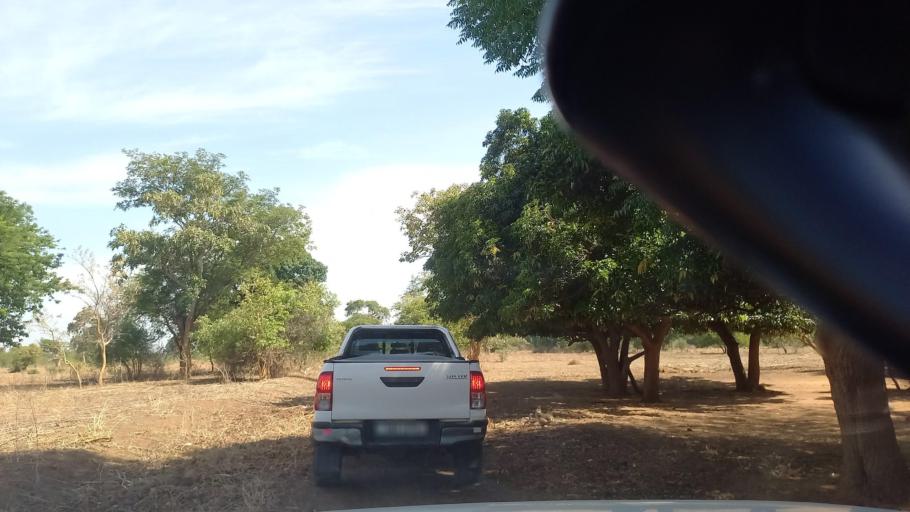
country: ZM
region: Southern
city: Mazabuka
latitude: -16.0352
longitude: 27.6230
